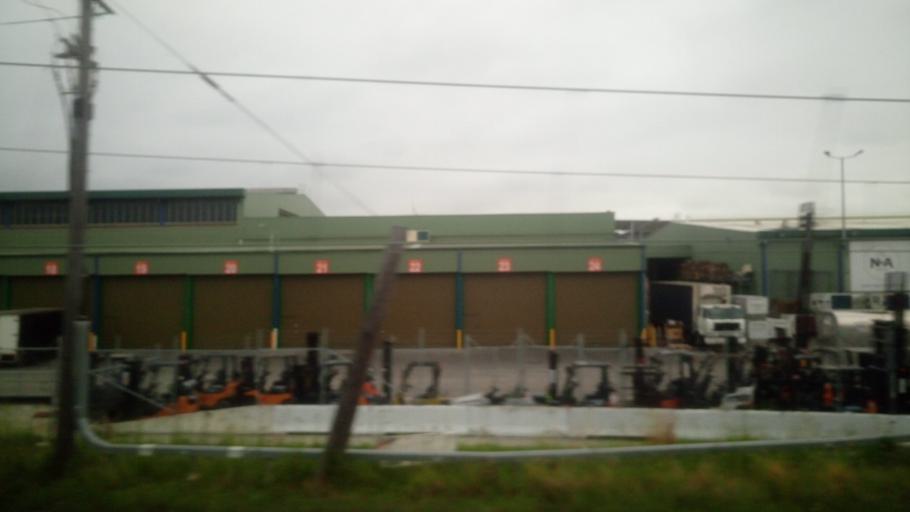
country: AU
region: New South Wales
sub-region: Strathfield
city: Homebush
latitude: -33.8646
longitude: 151.0694
